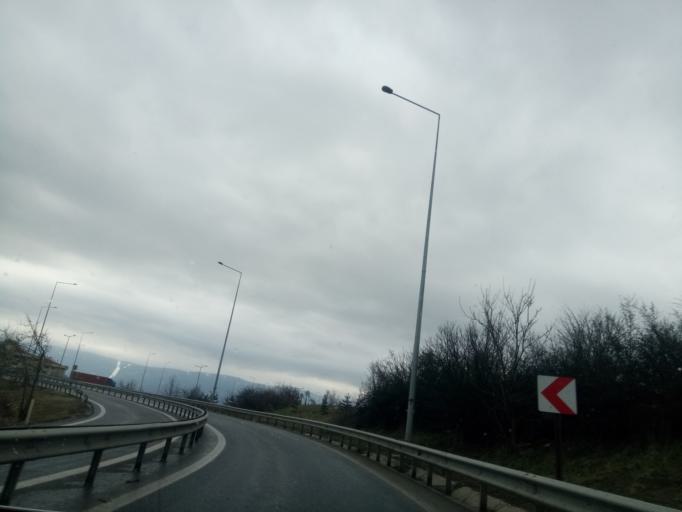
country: TR
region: Bolu
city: Bolu
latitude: 40.7168
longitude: 31.5228
